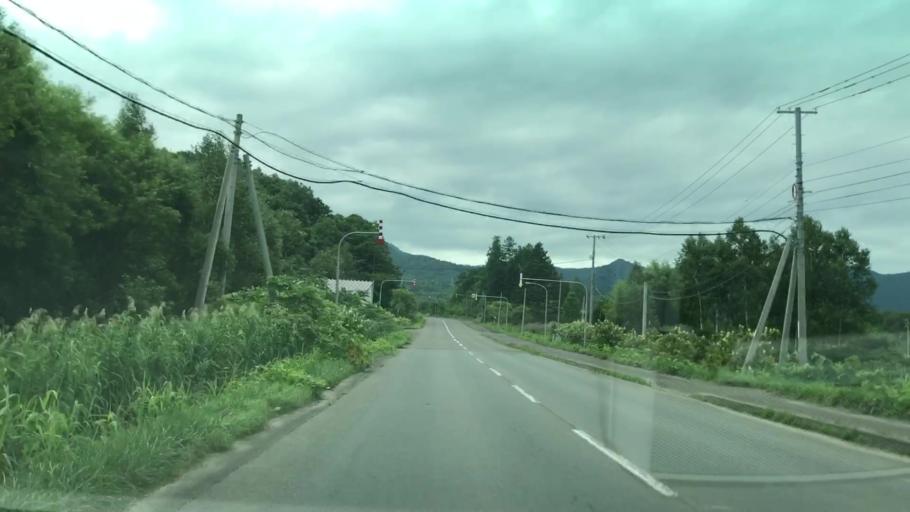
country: JP
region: Hokkaido
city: Yoichi
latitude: 43.0552
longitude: 140.8205
